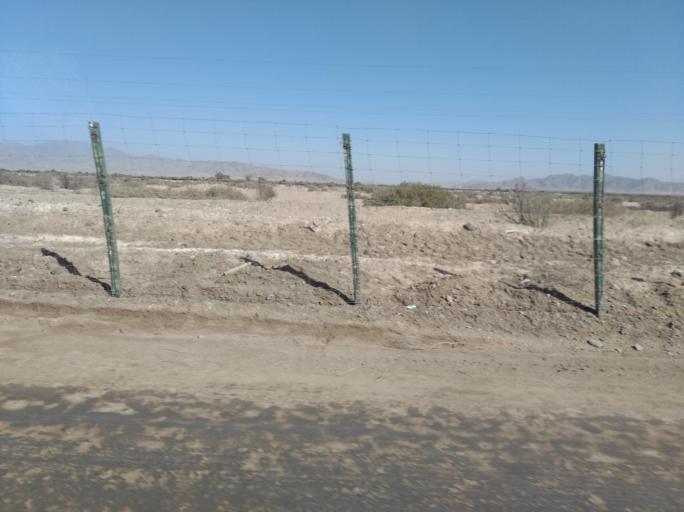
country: CL
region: Atacama
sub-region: Provincia de Copiapo
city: Copiapo
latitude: -27.3555
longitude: -70.6625
